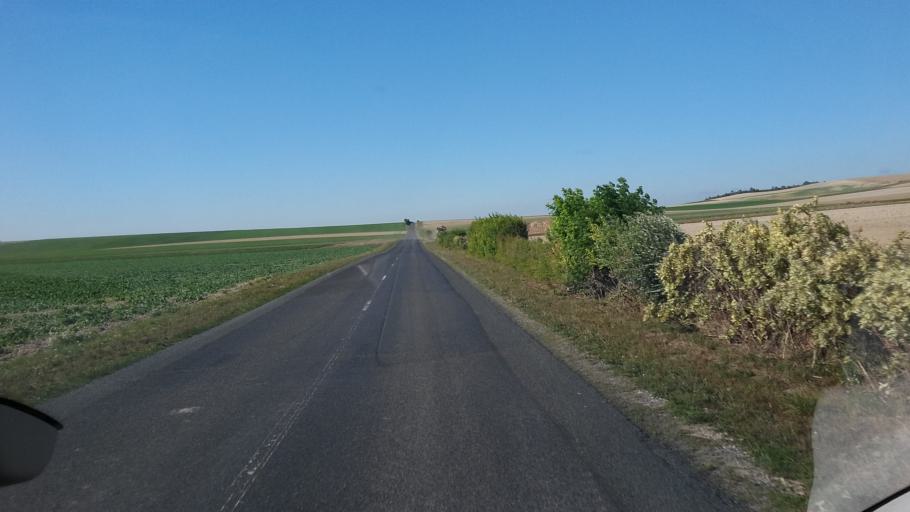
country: FR
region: Champagne-Ardenne
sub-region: Departement de la Marne
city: Connantre
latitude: 48.7563
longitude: 3.8797
